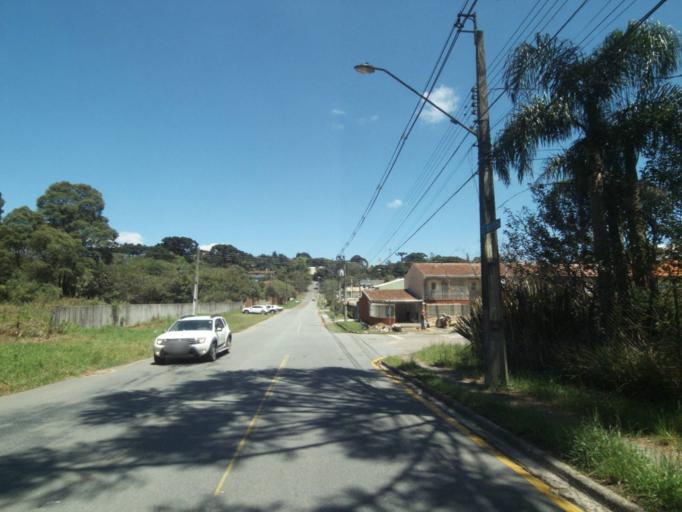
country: BR
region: Parana
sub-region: Curitiba
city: Curitiba
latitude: -25.3790
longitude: -49.2665
